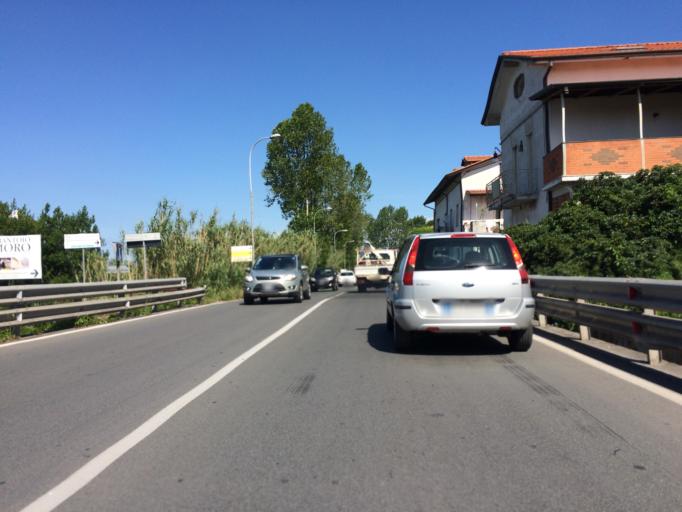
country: IT
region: Tuscany
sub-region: Provincia di Massa-Carrara
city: Borghetto-Melara
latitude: 44.0968
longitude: 9.9870
